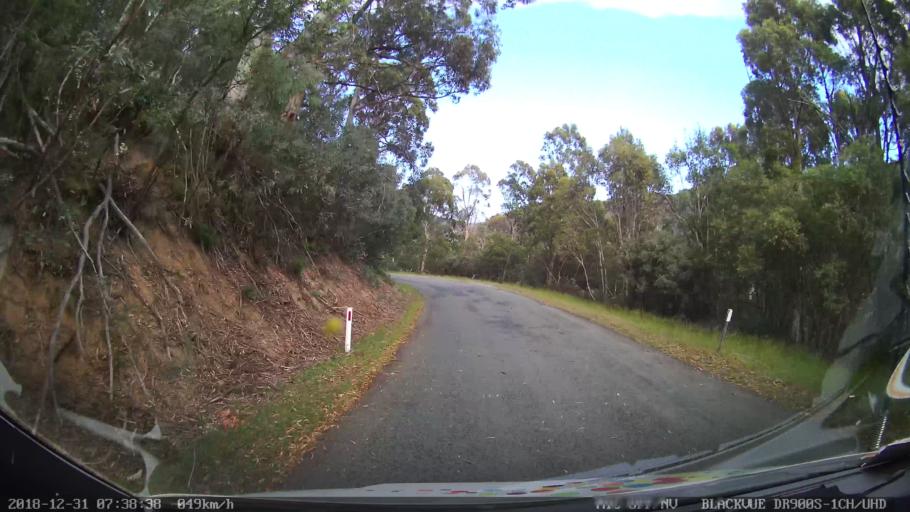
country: AU
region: New South Wales
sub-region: Snowy River
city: Jindabyne
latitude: -36.3487
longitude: 148.4272
